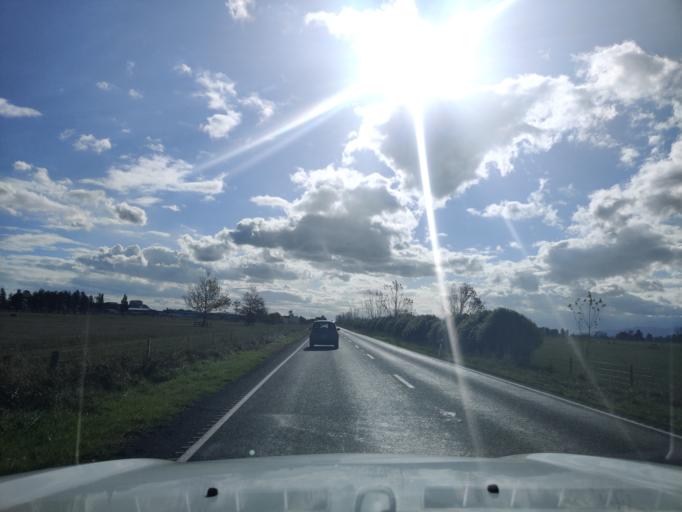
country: NZ
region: Waikato
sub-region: Hauraki District
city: Ngatea
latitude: -37.3056
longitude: 175.5623
